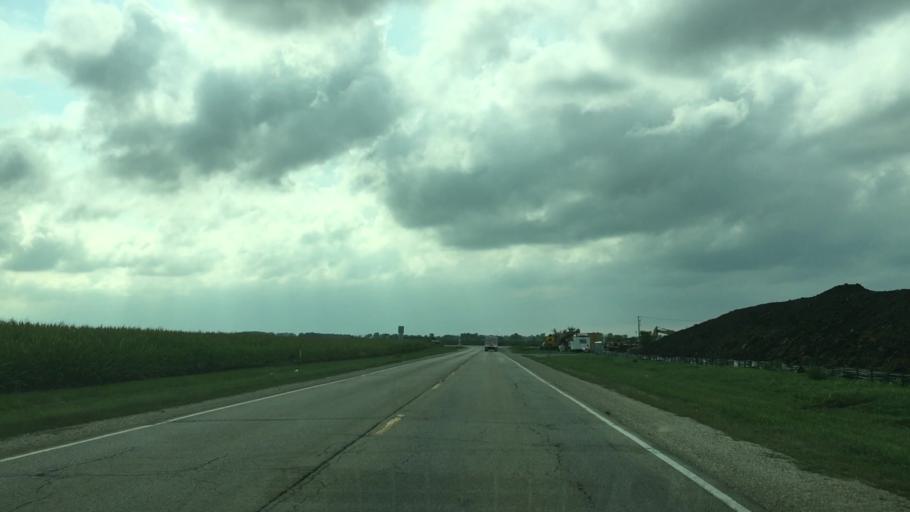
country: US
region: Illinois
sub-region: Ogle County
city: Rochelle
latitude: 41.8973
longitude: -89.0643
